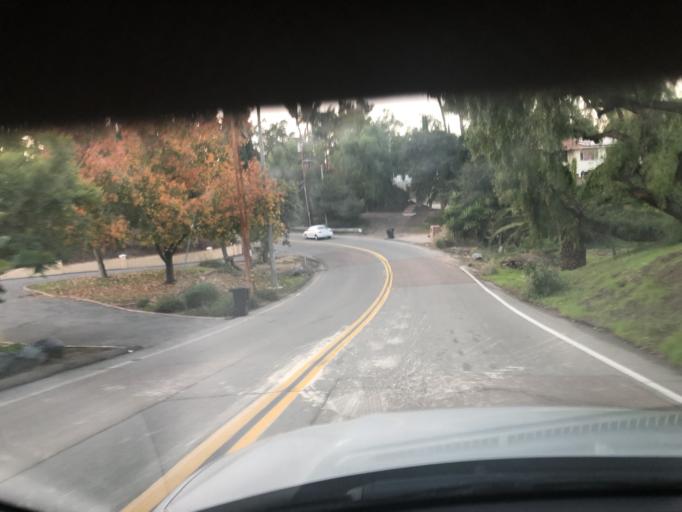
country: US
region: California
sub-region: San Diego County
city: Chula Vista
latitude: 32.6421
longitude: -117.0634
